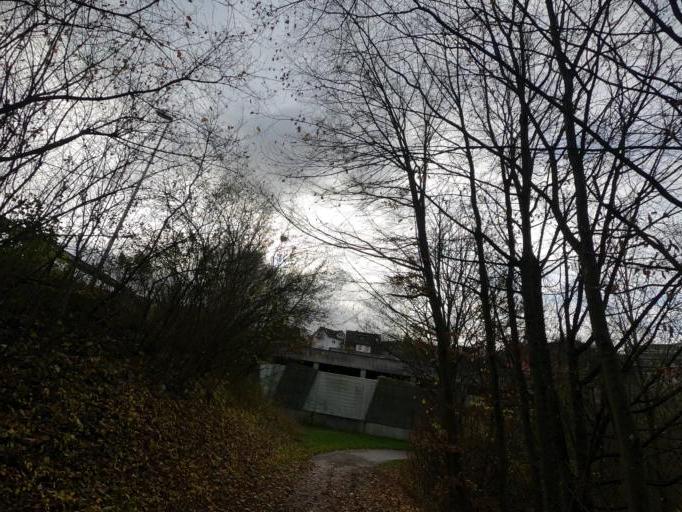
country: DE
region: Baden-Wuerttemberg
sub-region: Regierungsbezirk Stuttgart
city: Uhingen
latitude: 48.7035
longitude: 9.5837
